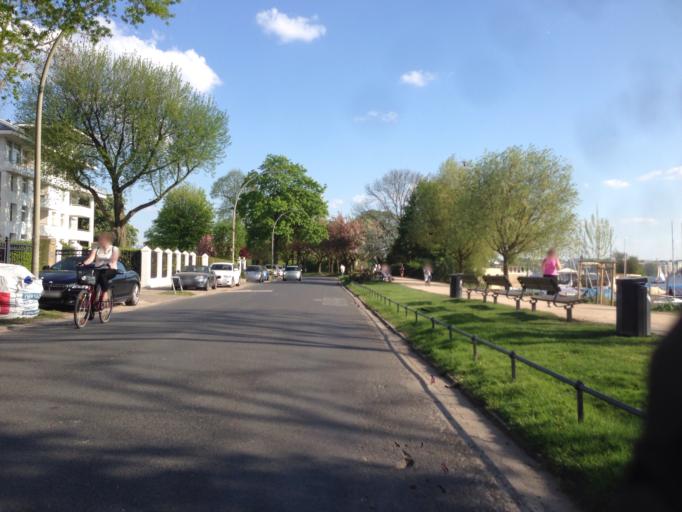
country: DE
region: Hamburg
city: Hamburg
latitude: 53.5709
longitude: 10.0095
